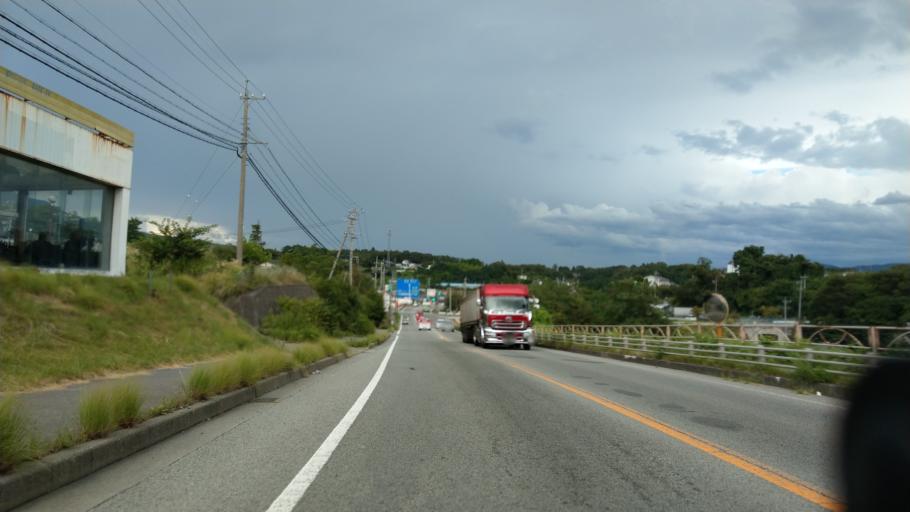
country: JP
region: Nagano
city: Komoro
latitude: 36.3131
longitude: 138.4544
